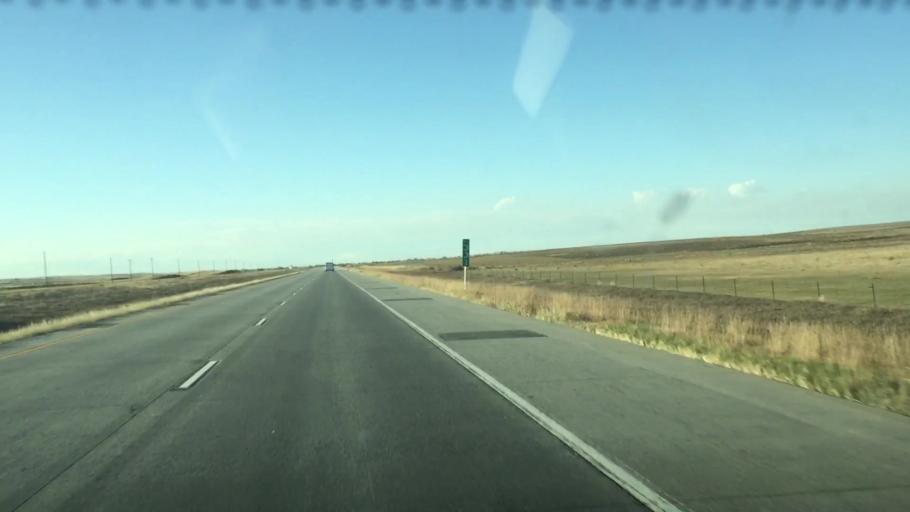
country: US
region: Colorado
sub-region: Arapahoe County
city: Byers
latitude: 39.5792
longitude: -104.0224
